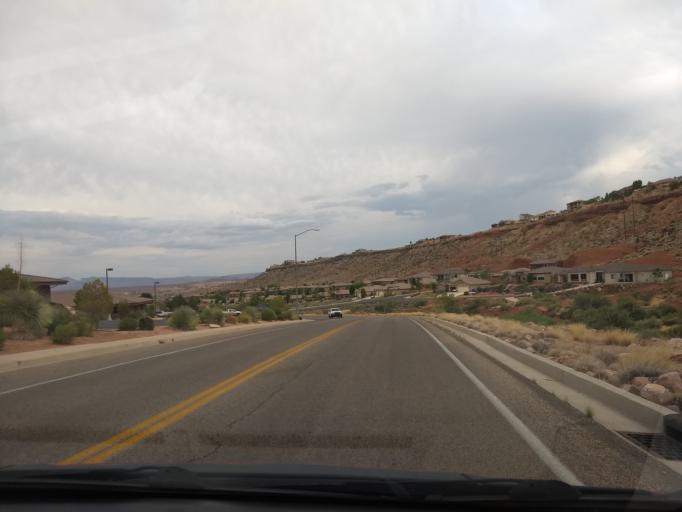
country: US
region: Utah
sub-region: Washington County
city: Saint George
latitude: 37.1131
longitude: -113.5477
